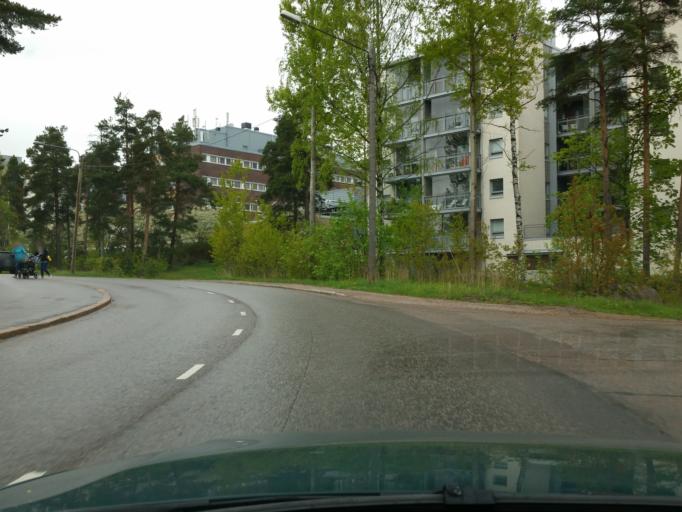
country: FI
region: Uusimaa
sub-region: Helsinki
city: Teekkarikylae
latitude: 60.2209
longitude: 24.8340
